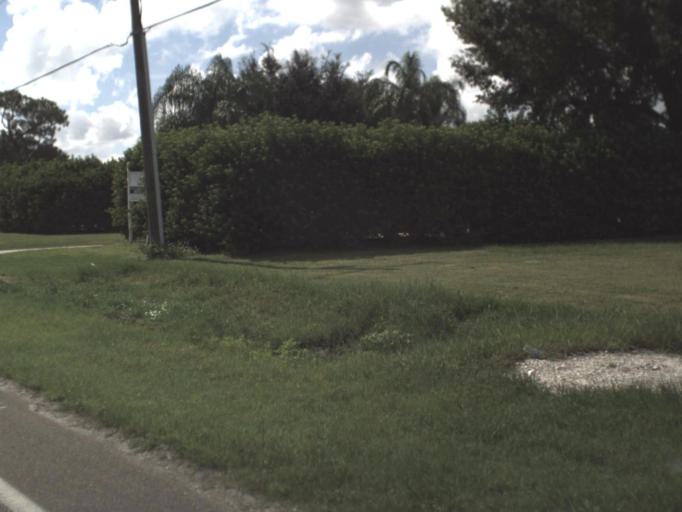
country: US
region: Florida
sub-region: Hardee County
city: Zolfo Springs
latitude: 27.4951
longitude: -81.8294
